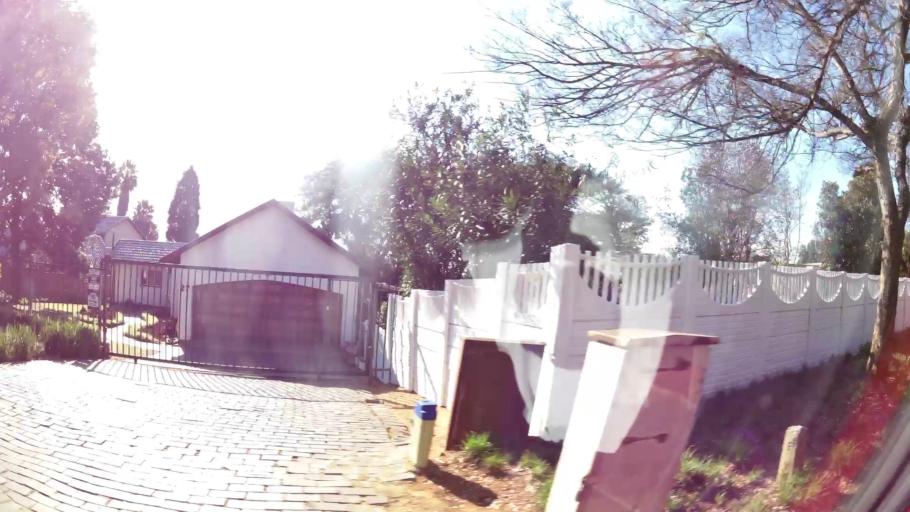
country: ZA
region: Gauteng
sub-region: City of Johannesburg Metropolitan Municipality
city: Roodepoort
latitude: -26.1080
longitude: 27.9545
